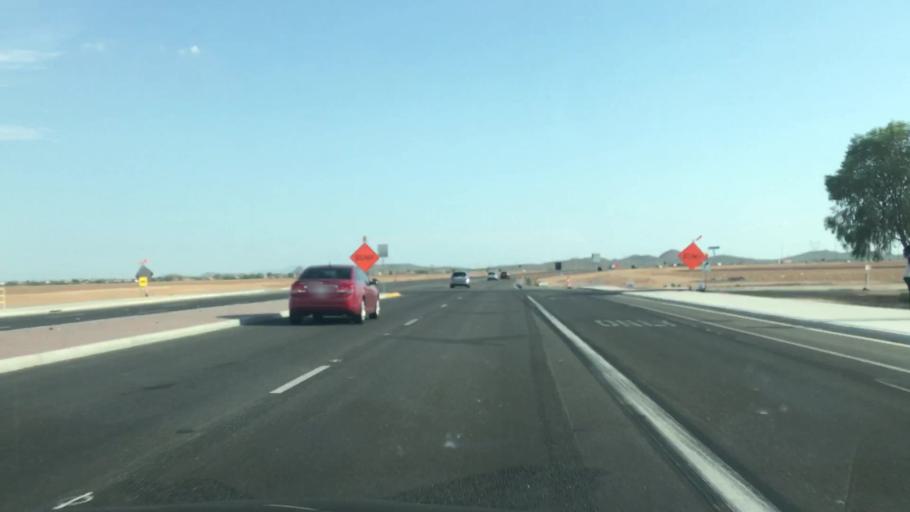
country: US
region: Arizona
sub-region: Pinal County
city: San Tan Valley
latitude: 33.1552
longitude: -111.5446
